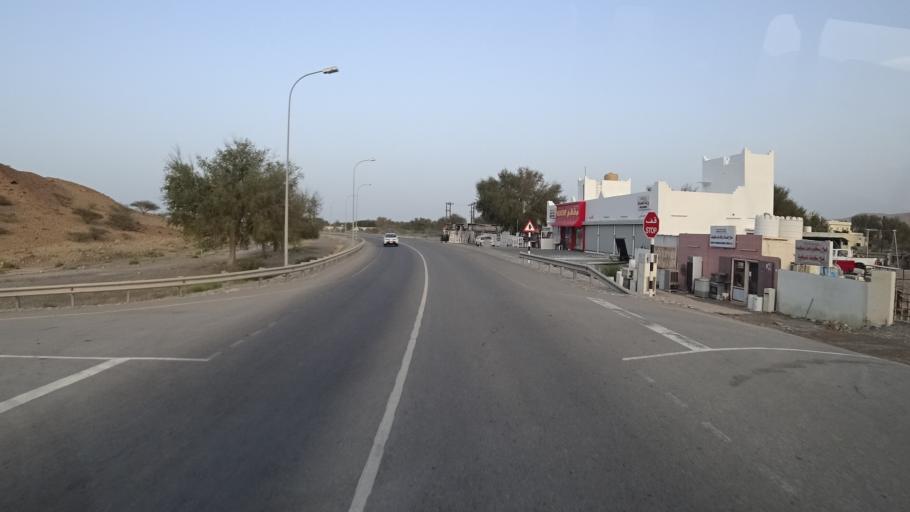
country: OM
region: Muhafazat Masqat
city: Muscat
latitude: 23.2047
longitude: 58.9519
